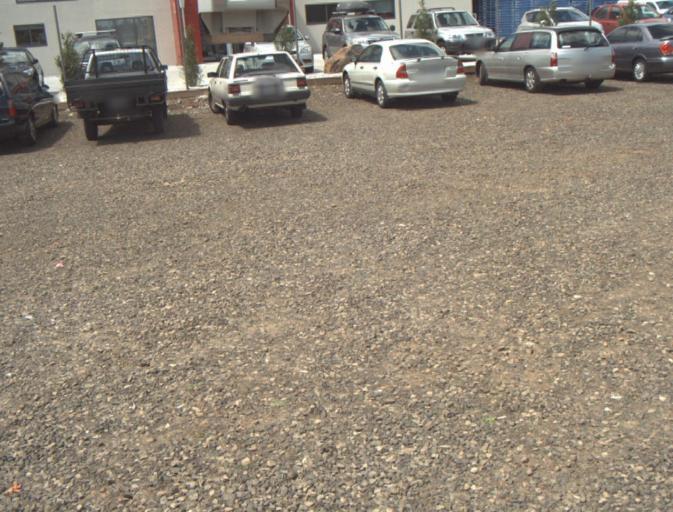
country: AU
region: Tasmania
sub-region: Launceston
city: Launceston
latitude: -41.4243
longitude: 147.1216
